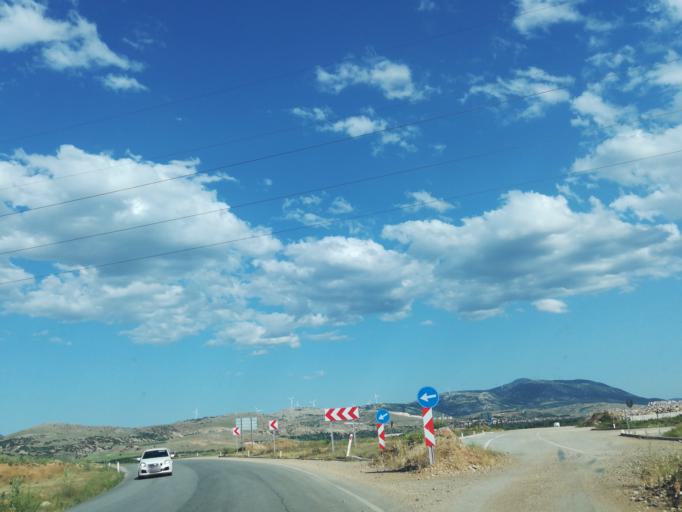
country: TR
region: Afyonkarahisar
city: Dinar
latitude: 38.1016
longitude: 30.1300
